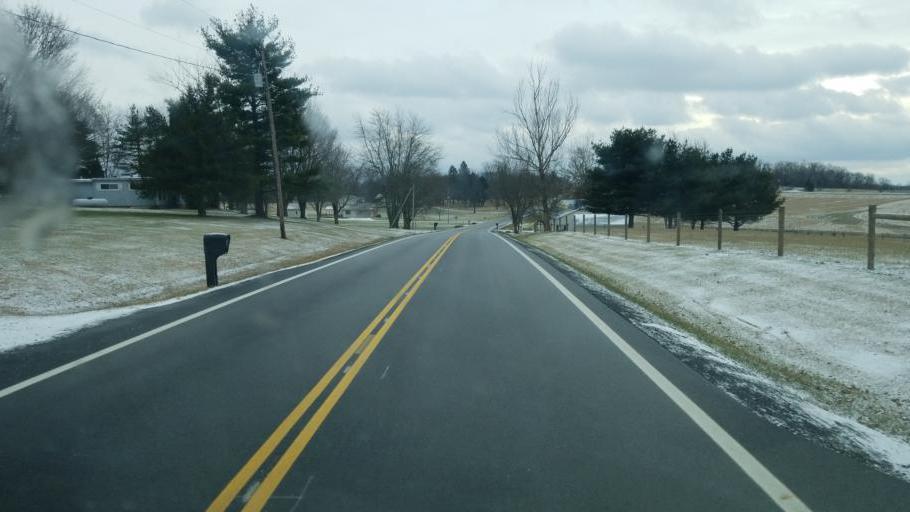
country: US
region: Ohio
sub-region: Knox County
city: Gambier
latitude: 40.3486
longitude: -82.4363
